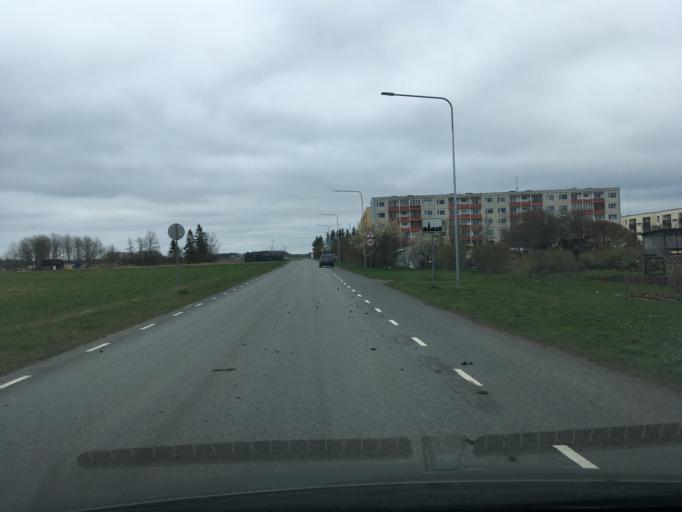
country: EE
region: Harju
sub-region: Rae vald
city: Vaida
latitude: 59.2896
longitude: 24.9788
